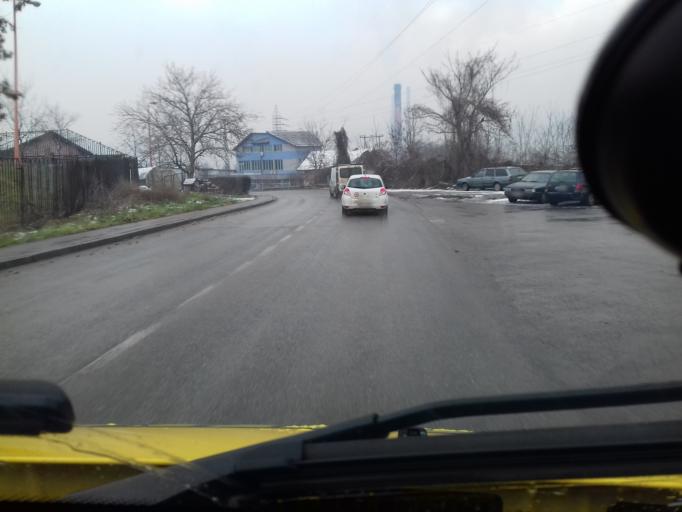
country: BA
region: Federation of Bosnia and Herzegovina
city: Zenica
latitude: 44.2177
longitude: 17.8927
